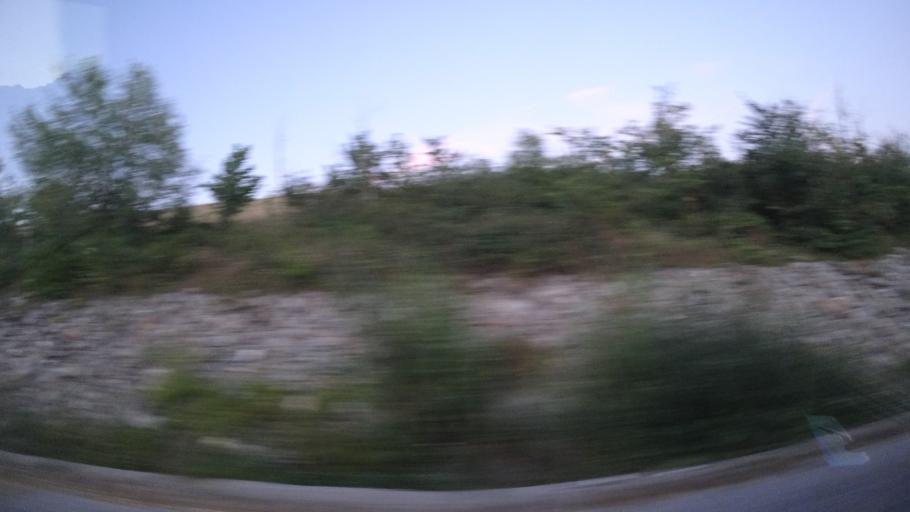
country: FR
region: Midi-Pyrenees
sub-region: Departement de l'Aveyron
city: Millau
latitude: 44.1236
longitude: 3.0561
